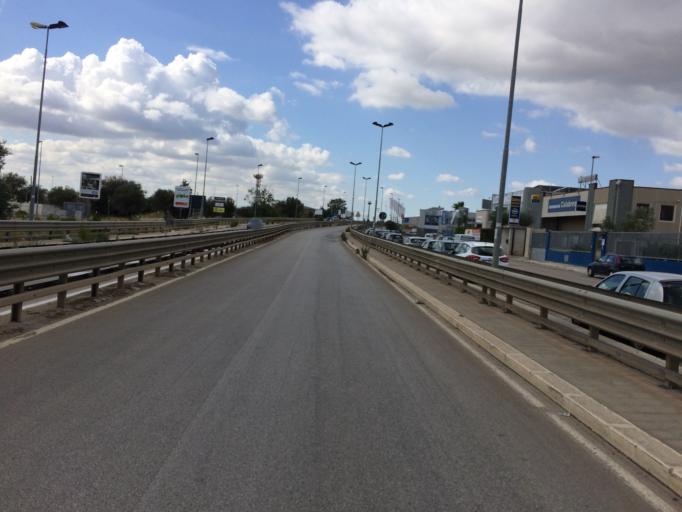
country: IT
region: Apulia
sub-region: Provincia di Bari
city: Bari
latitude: 41.1015
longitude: 16.8348
